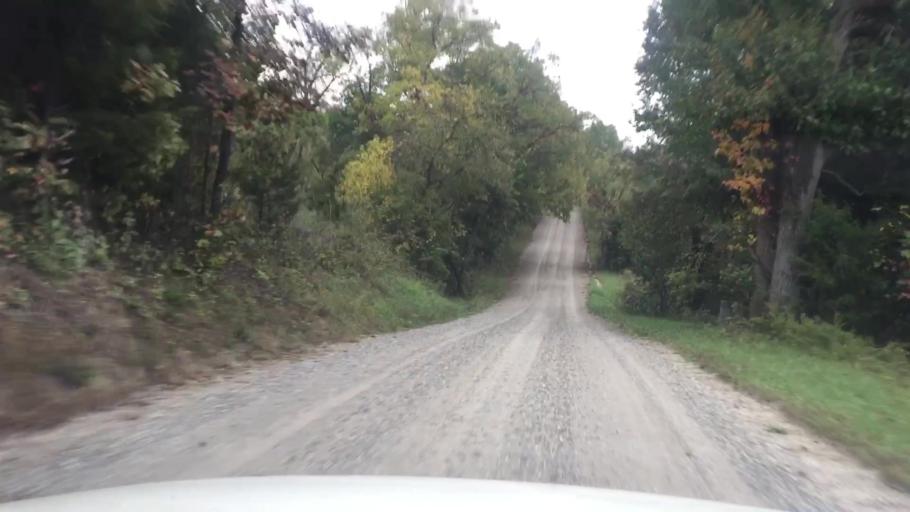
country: US
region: Missouri
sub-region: Boone County
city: Ashland
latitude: 38.8221
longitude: -92.3360
